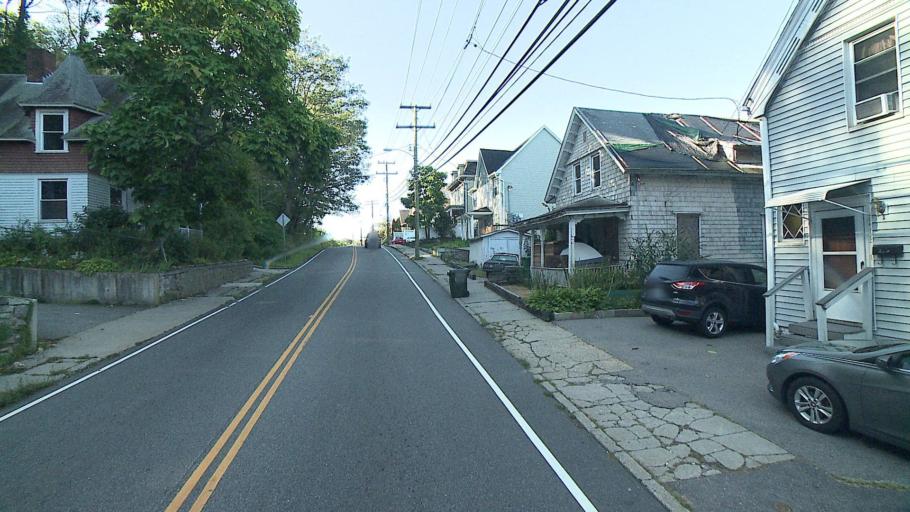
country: US
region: Connecticut
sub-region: New London County
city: Norwich
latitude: 41.5161
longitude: -72.0748
